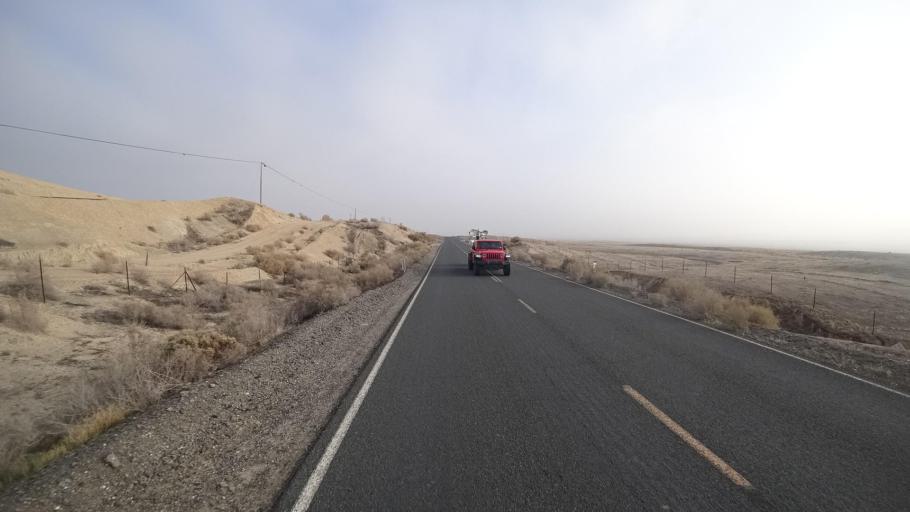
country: US
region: California
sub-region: Kern County
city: Ford City
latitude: 35.2432
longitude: -119.4554
